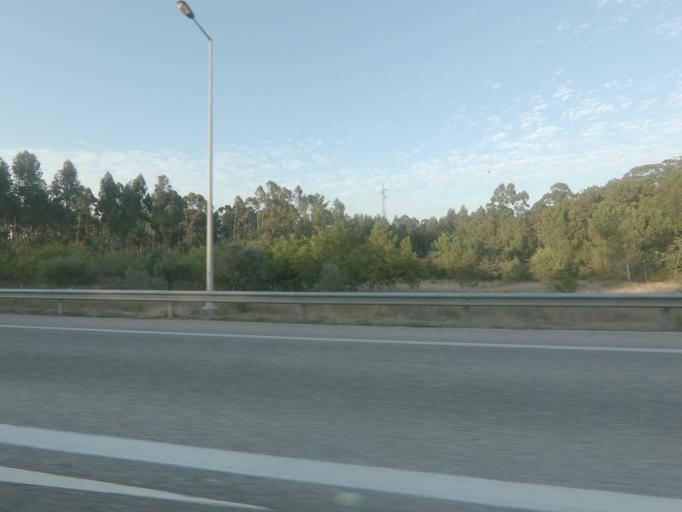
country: PT
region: Santarem
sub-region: Ourem
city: Fatima
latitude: 39.6225
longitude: -8.6931
